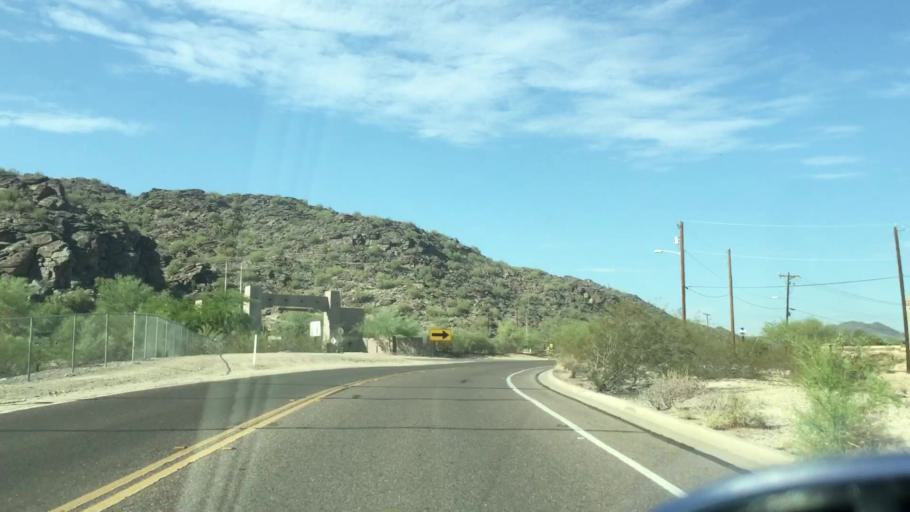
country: US
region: Arizona
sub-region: Maricopa County
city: Guadalupe
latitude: 33.3638
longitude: -112.0416
